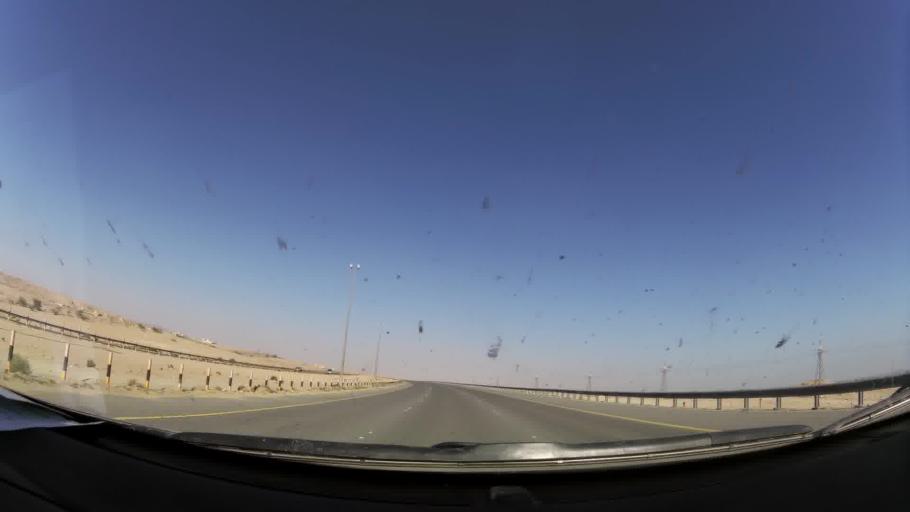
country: KW
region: Muhafazat al Jahra'
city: Al Jahra'
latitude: 29.4497
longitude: 47.7562
